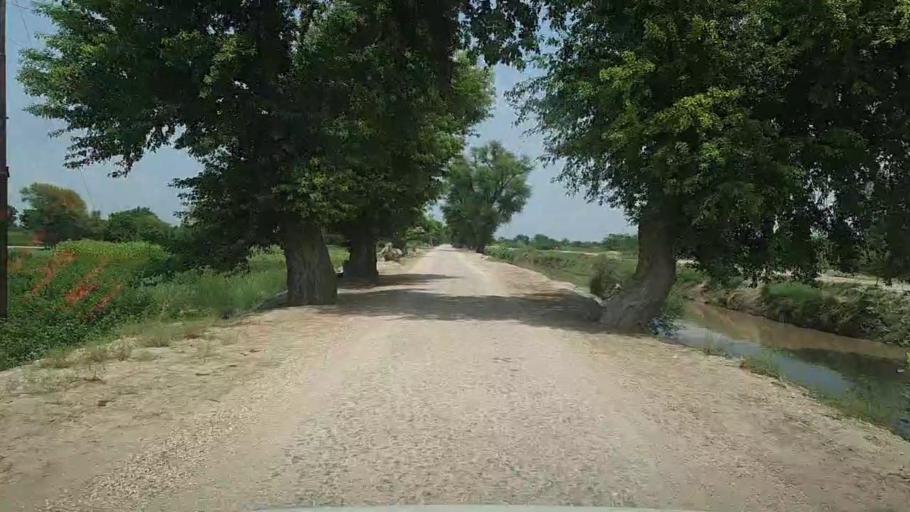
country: PK
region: Sindh
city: Karaundi
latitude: 26.9054
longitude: 68.3318
